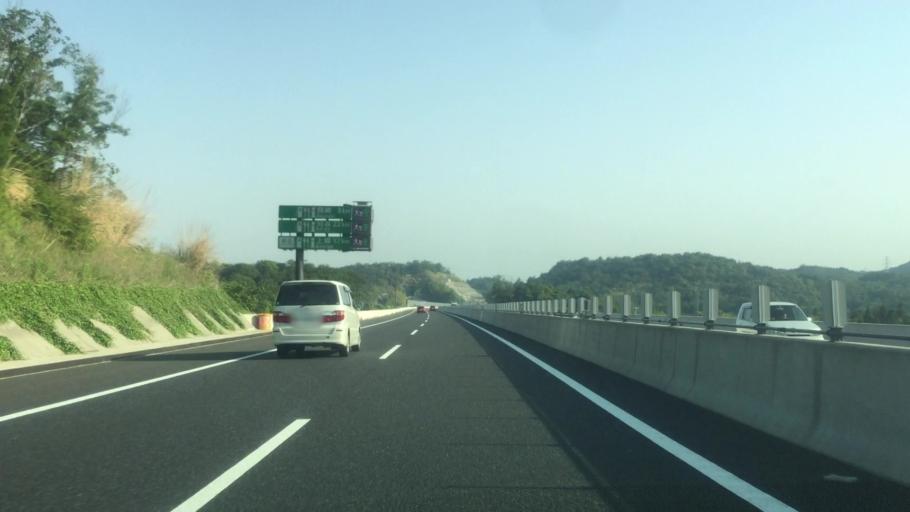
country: JP
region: Aichi
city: Okazaki
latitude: 35.0032
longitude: 137.2303
